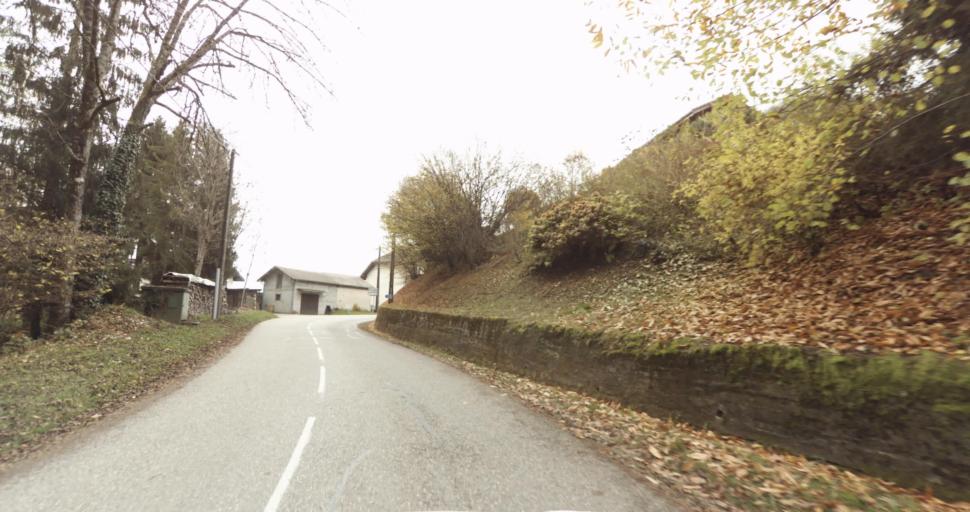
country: FR
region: Rhone-Alpes
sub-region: Departement de la Haute-Savoie
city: Saint-Jorioz
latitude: 45.8294
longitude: 6.1408
